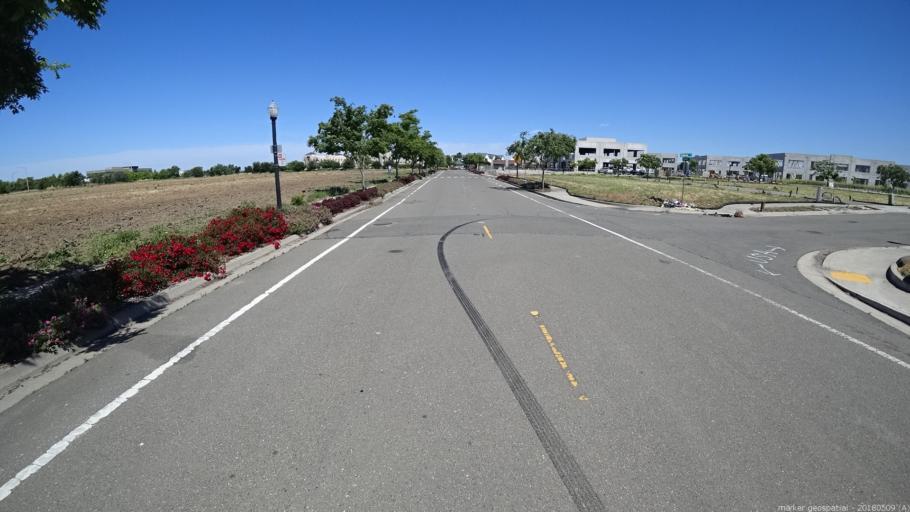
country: US
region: California
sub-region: Yolo County
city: West Sacramento
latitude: 38.6520
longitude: -121.5285
